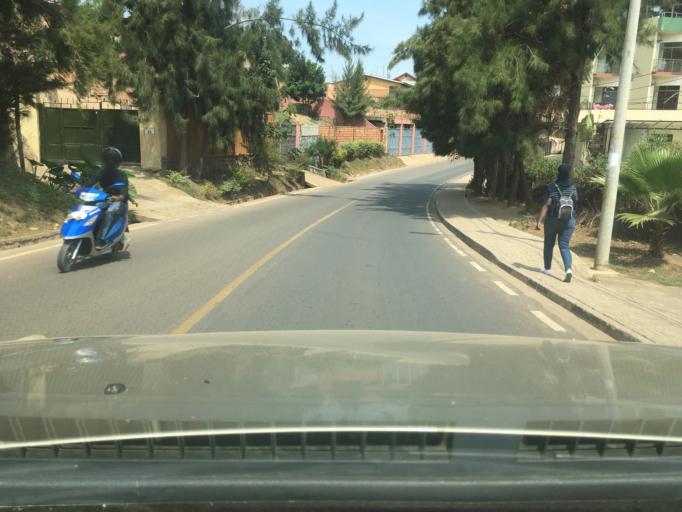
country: RW
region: Kigali
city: Kigali
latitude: -1.9617
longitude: 30.1041
